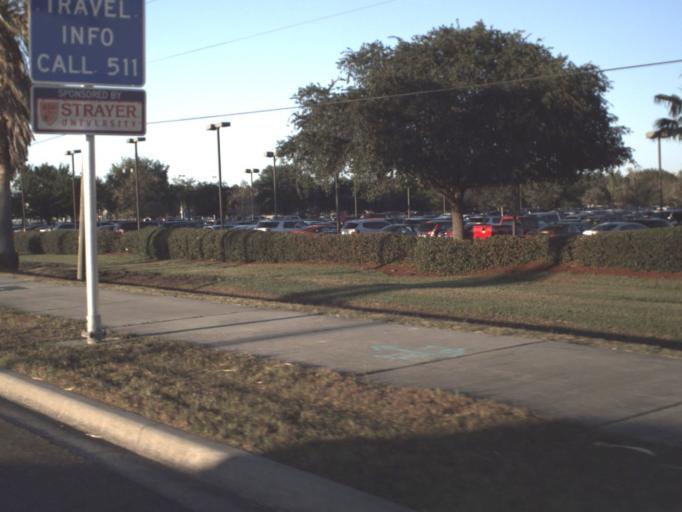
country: US
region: Florida
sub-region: Orange County
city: Conway
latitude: 28.4706
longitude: -81.3099
